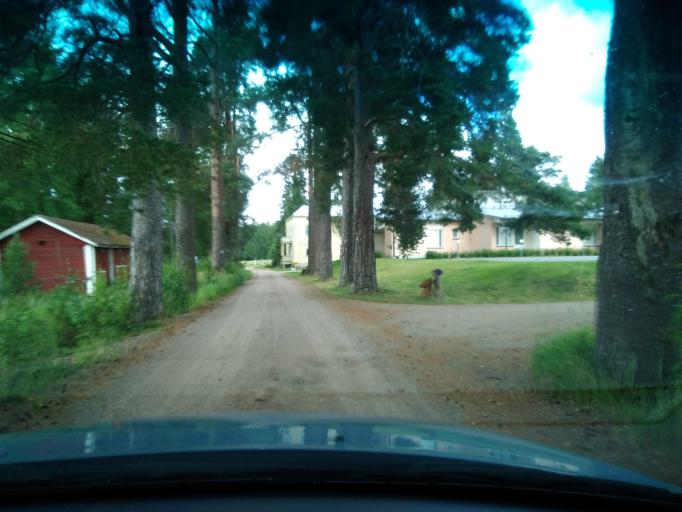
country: FI
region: Central Finland
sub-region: Saarijaervi-Viitasaari
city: Saarijaervi
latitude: 62.7377
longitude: 25.1824
